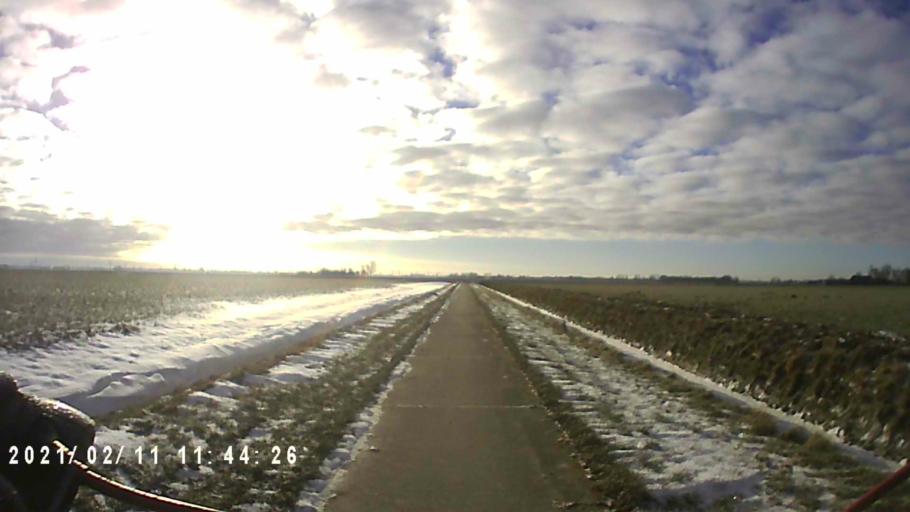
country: NL
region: Groningen
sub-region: Gemeente Zuidhorn
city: Aduard
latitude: 53.2842
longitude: 6.4533
